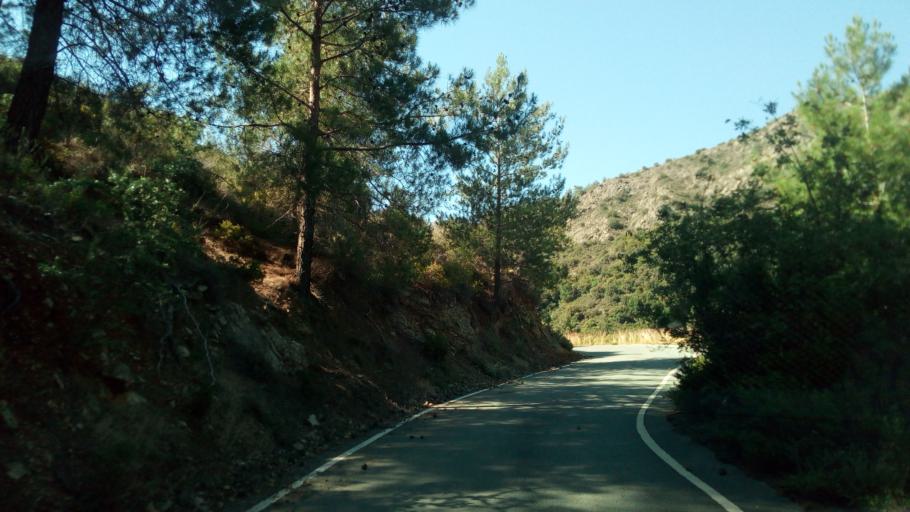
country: CY
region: Lefkosia
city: Lythrodontas
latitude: 34.8886
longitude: 33.2154
